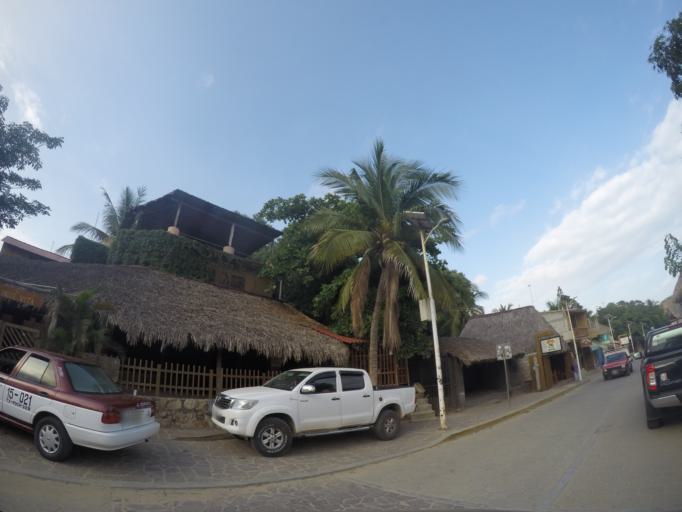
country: MX
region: Oaxaca
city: Santa Maria Tonameca
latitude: 15.6680
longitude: -96.5557
